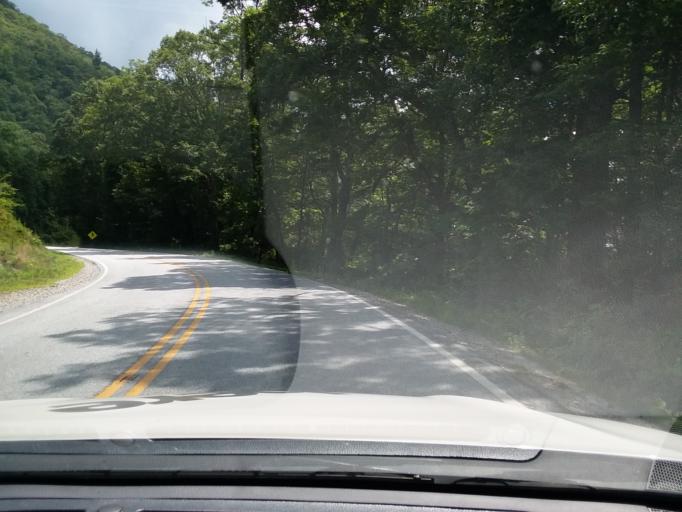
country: US
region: Georgia
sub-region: Rabun County
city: Mountain City
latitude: 35.0287
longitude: -83.2846
